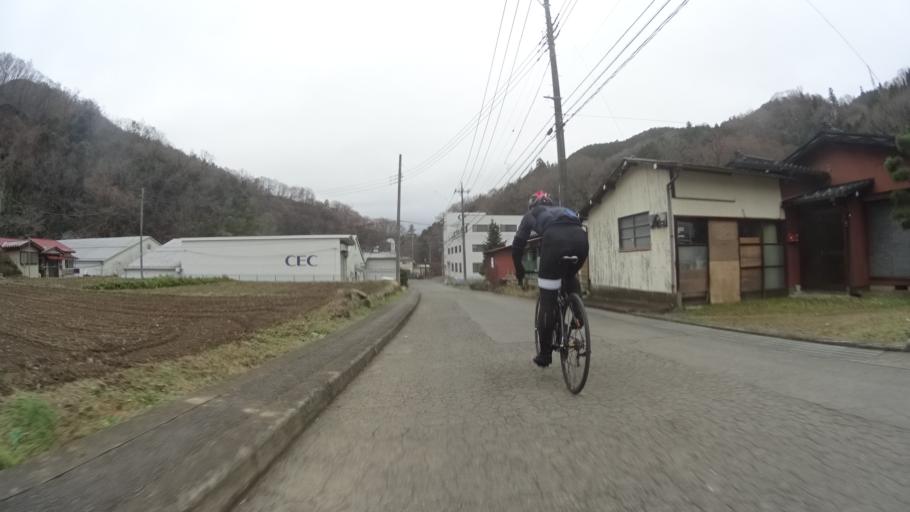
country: JP
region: Yamanashi
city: Uenohara
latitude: 35.6215
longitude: 139.1537
